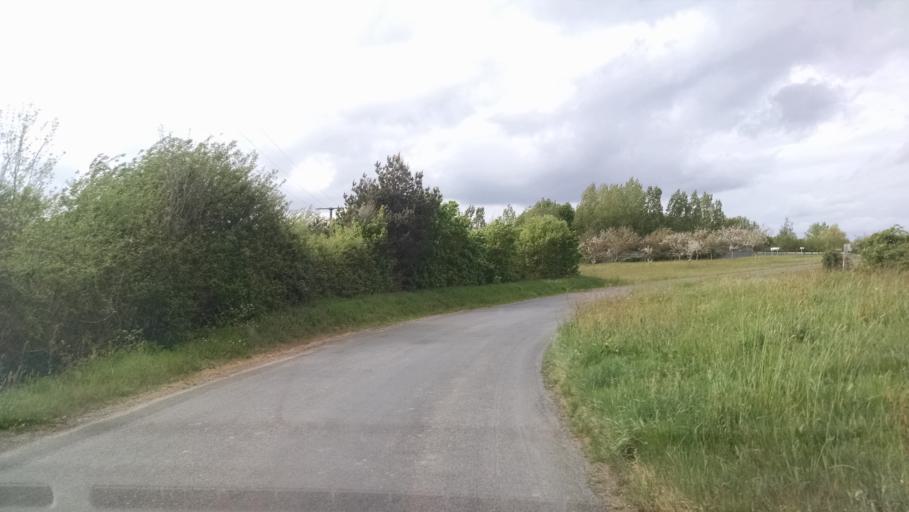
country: FR
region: Pays de la Loire
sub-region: Departement de la Vendee
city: Saint-Hilaire-de-Loulay
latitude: 46.9905
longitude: -1.3501
